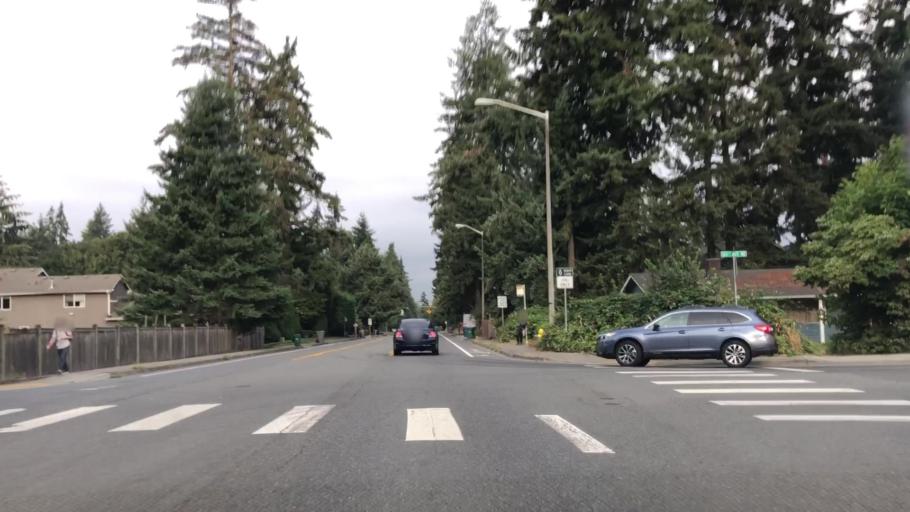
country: US
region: Washington
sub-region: King County
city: Kirkland
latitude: 47.6681
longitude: -122.1745
